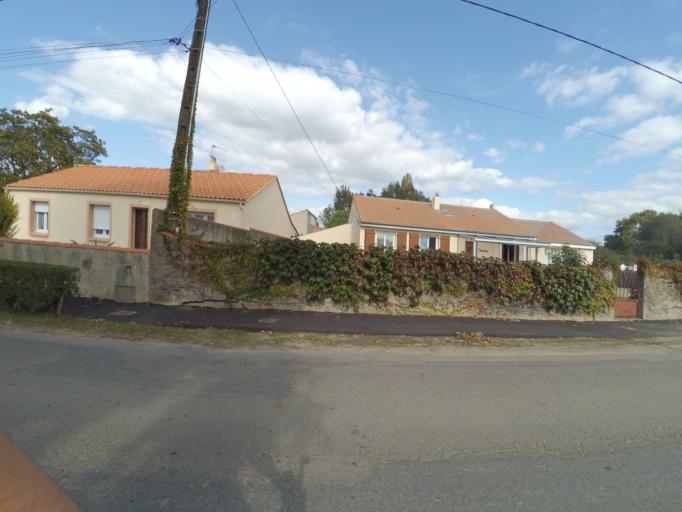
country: FR
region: Pays de la Loire
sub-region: Departement de la Loire-Atlantique
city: Chemere
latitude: 47.1197
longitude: -1.9108
